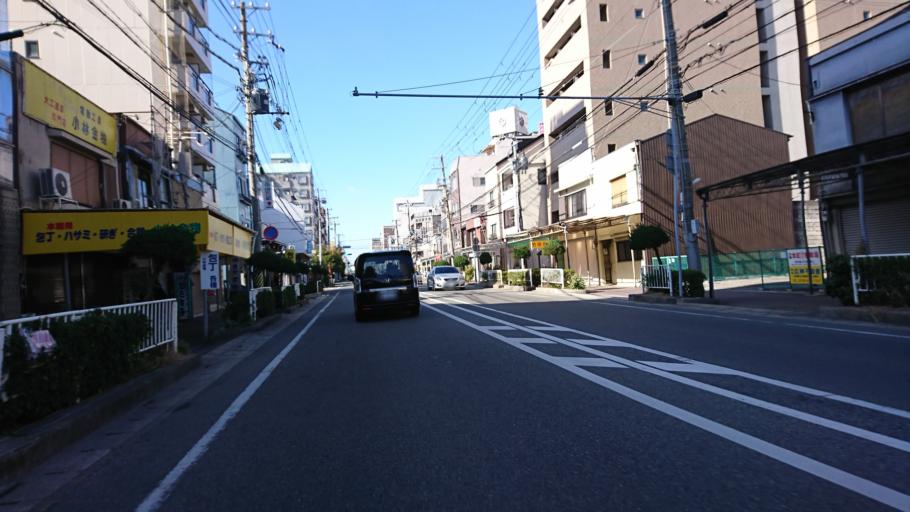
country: JP
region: Hyogo
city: Akashi
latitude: 34.6462
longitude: 134.9892
